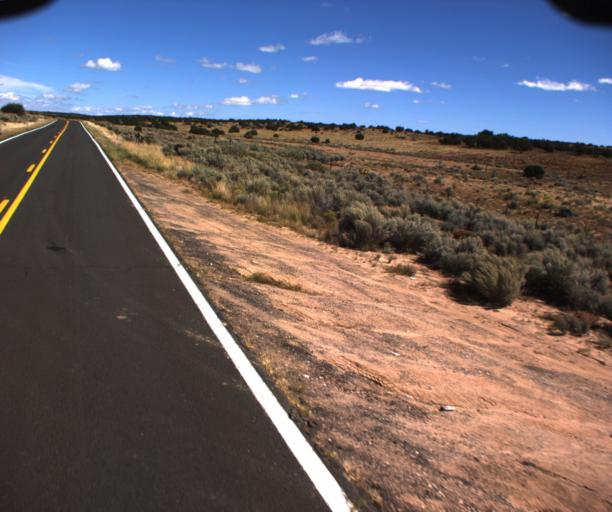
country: US
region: Arizona
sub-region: Apache County
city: Houck
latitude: 34.9375
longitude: -109.1838
